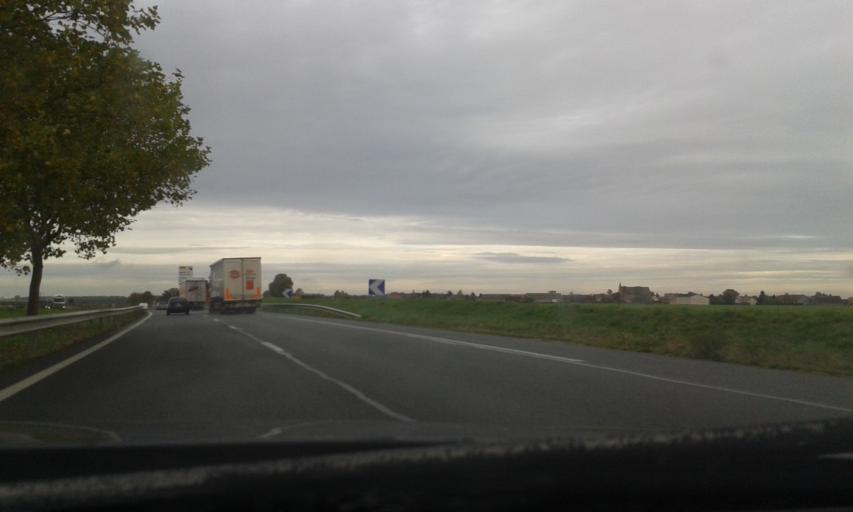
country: FR
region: Centre
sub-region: Departement d'Eure-et-Loir
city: Luray
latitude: 48.6681
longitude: 1.3895
